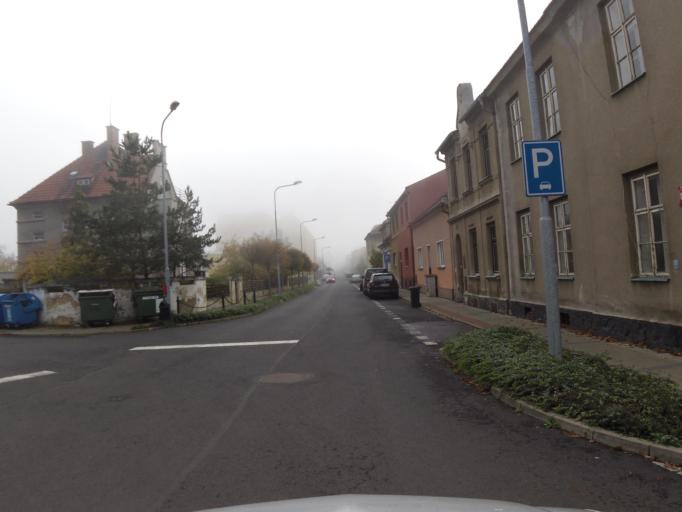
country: CZ
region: Ustecky
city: Zatec
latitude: 50.3227
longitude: 13.5526
